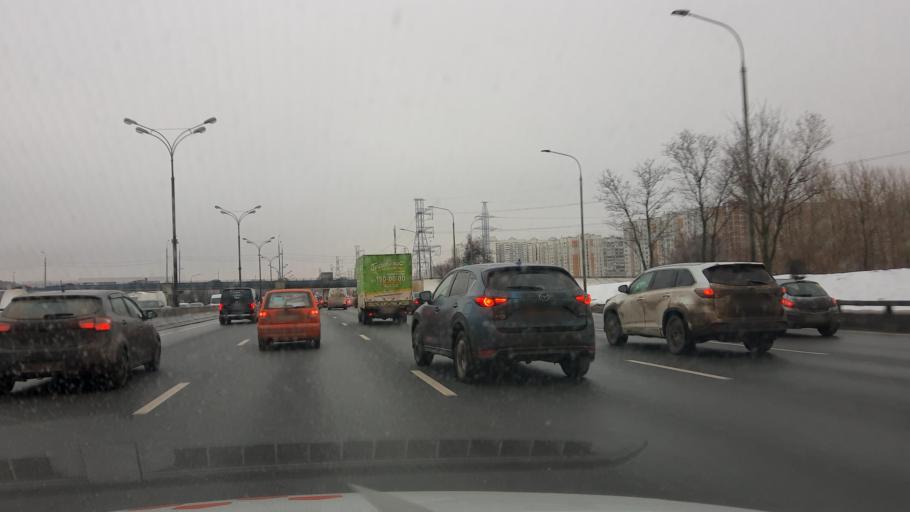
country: RU
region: Moscow
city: Chertanovo Yuzhnoye
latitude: 55.5813
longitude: 37.5694
